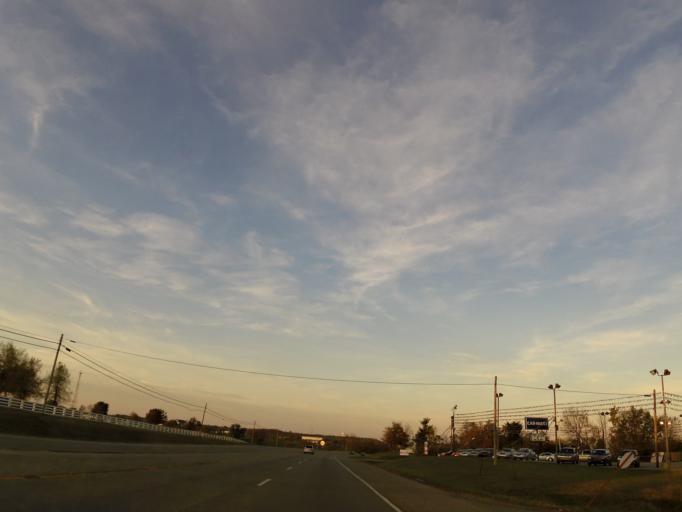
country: US
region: Kentucky
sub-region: Jessamine County
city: Nicholasville
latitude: 37.9202
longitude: -84.5557
